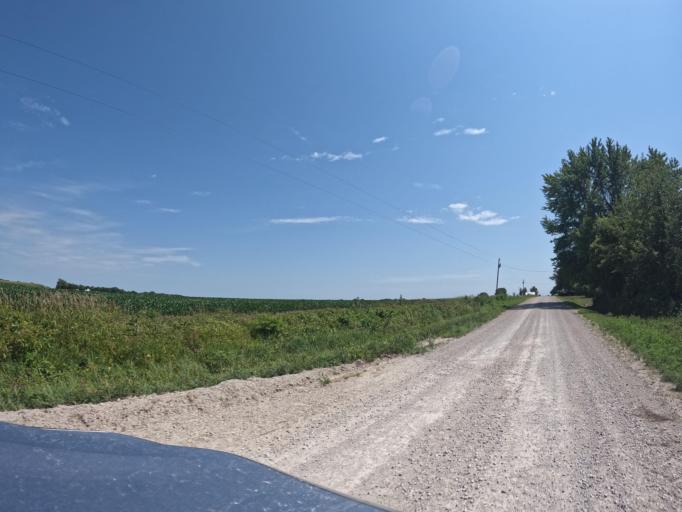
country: US
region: Iowa
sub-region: Henry County
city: Mount Pleasant
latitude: 40.9052
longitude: -91.6316
